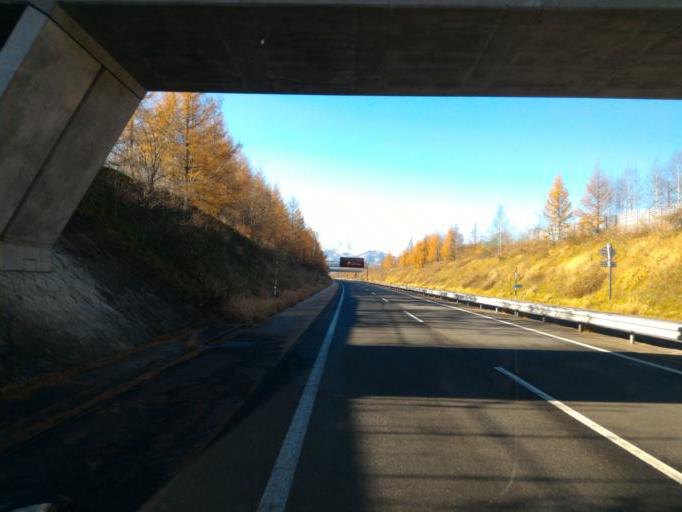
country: JP
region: Hokkaido
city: Otofuke
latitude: 42.9764
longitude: 142.9221
